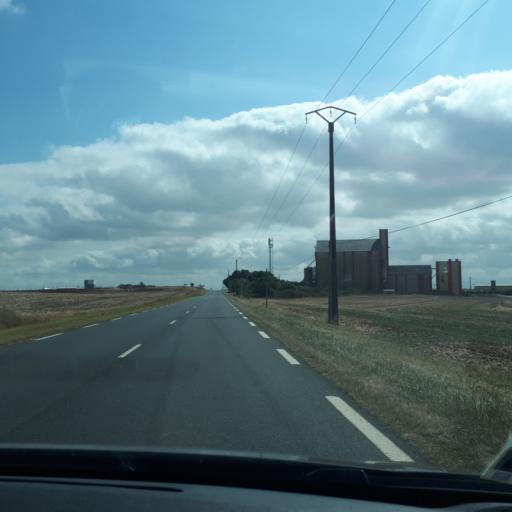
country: FR
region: Centre
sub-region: Departement du Loir-et-Cher
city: Oucques
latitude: 47.9042
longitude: 1.3744
